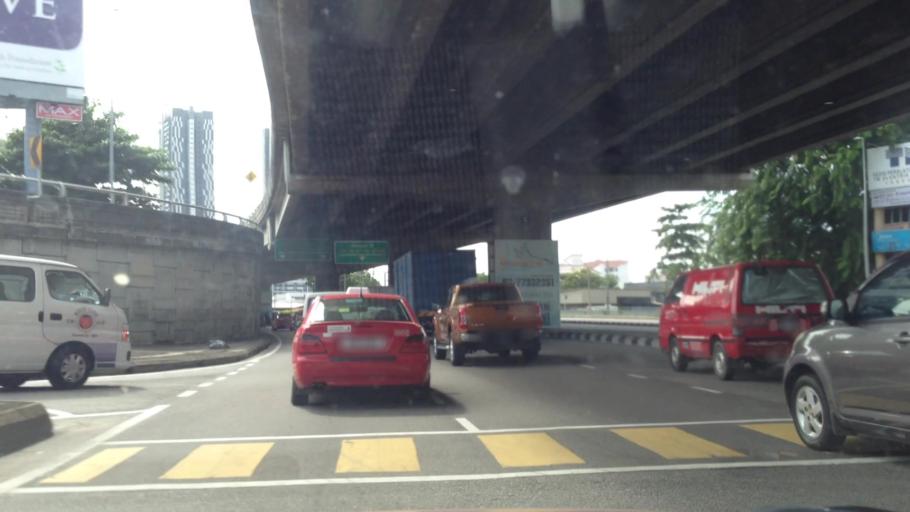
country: MY
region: Selangor
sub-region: Petaling
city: Petaling Jaya
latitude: 3.0817
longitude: 101.6558
